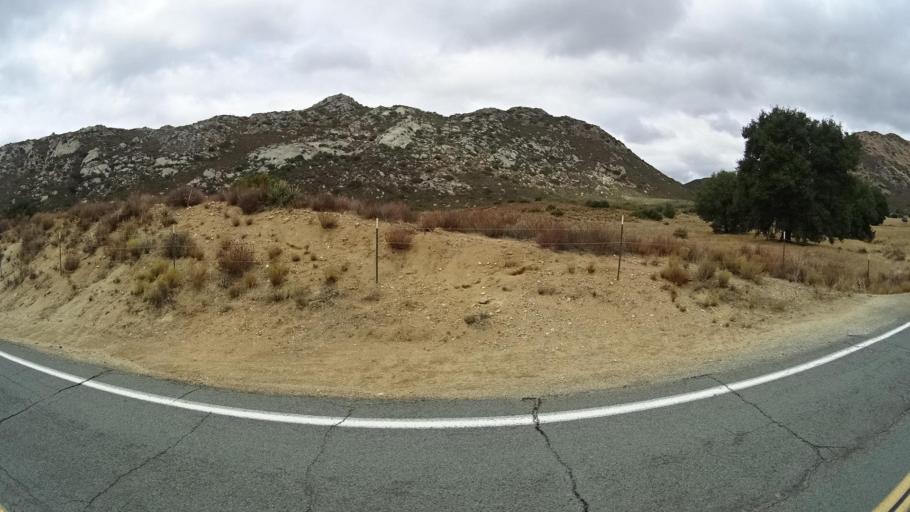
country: US
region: California
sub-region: San Diego County
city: Pine Valley
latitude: 32.7261
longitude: -116.4630
